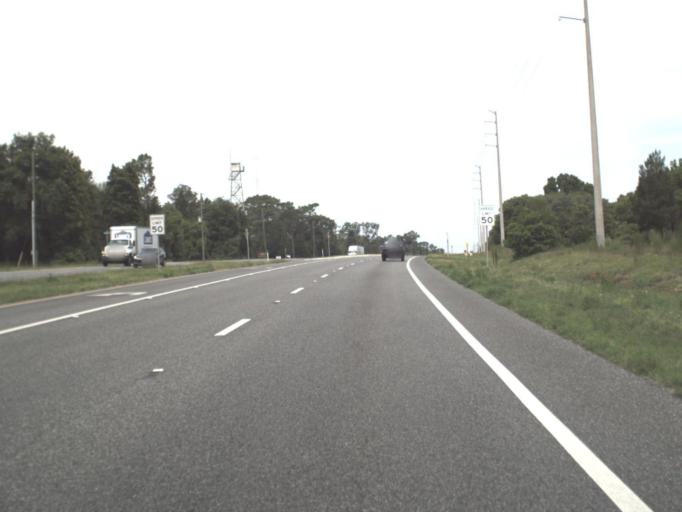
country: US
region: Florida
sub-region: Putnam County
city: Interlachen
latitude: 29.6264
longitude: -81.7927
